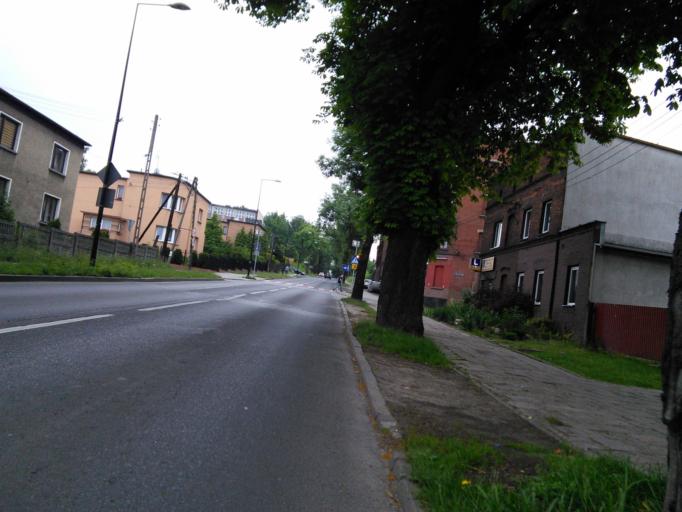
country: PL
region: Silesian Voivodeship
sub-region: Piekary Slaskie
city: Brzeziny Slaskie
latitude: 50.3661
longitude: 18.9824
